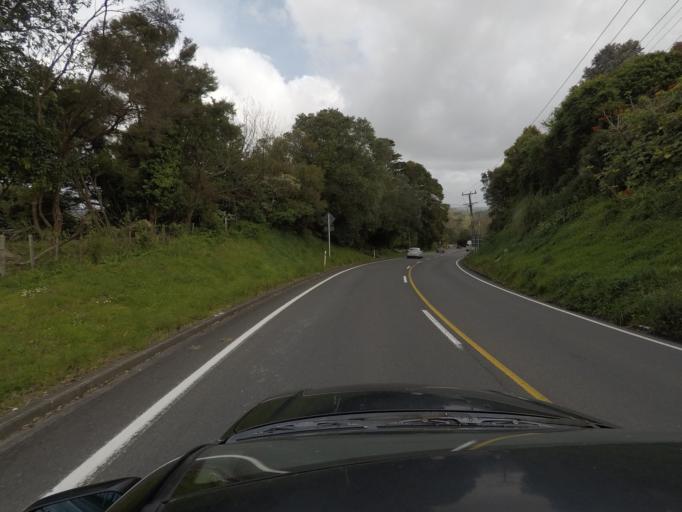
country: NZ
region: Auckland
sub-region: Auckland
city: Pakuranga
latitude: -36.9219
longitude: 174.9332
